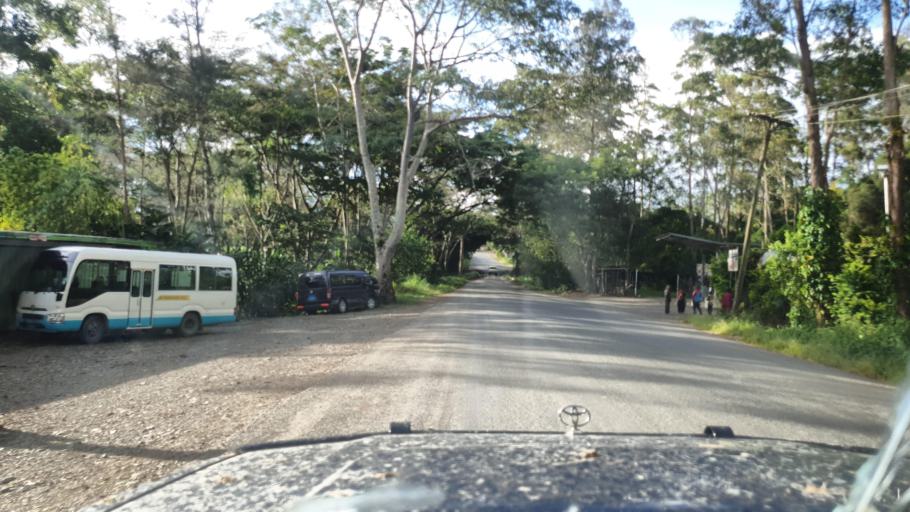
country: PG
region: Jiwaka
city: Minj
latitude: -5.8450
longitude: 144.6218
